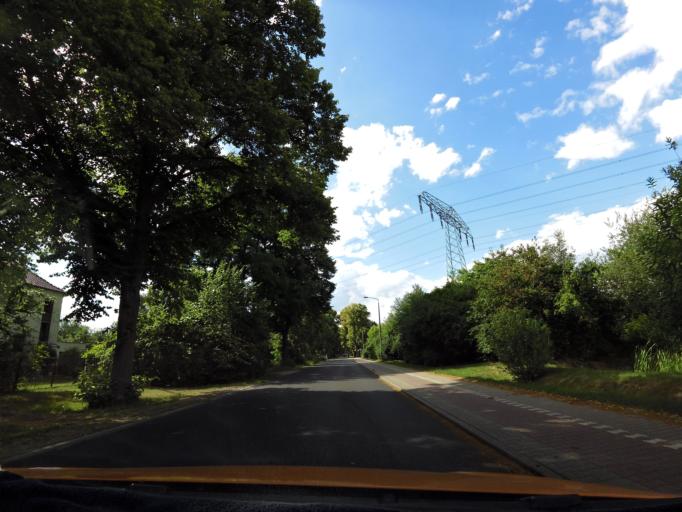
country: DE
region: Berlin
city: Lichtenrade
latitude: 52.3537
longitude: 13.4164
